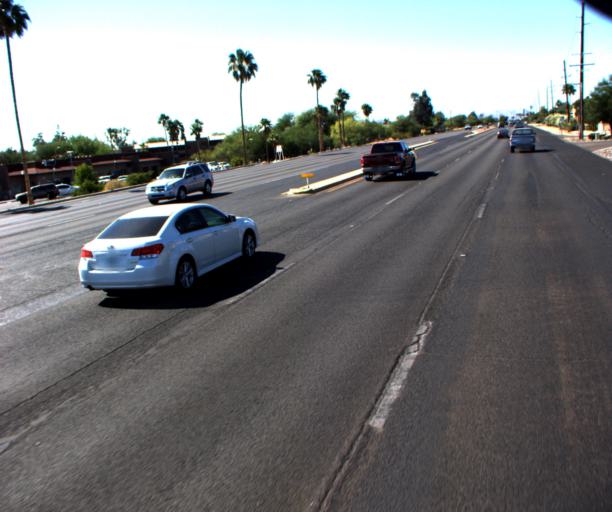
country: US
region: Arizona
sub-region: Pima County
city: Casas Adobes
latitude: 32.3237
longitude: -110.9749
